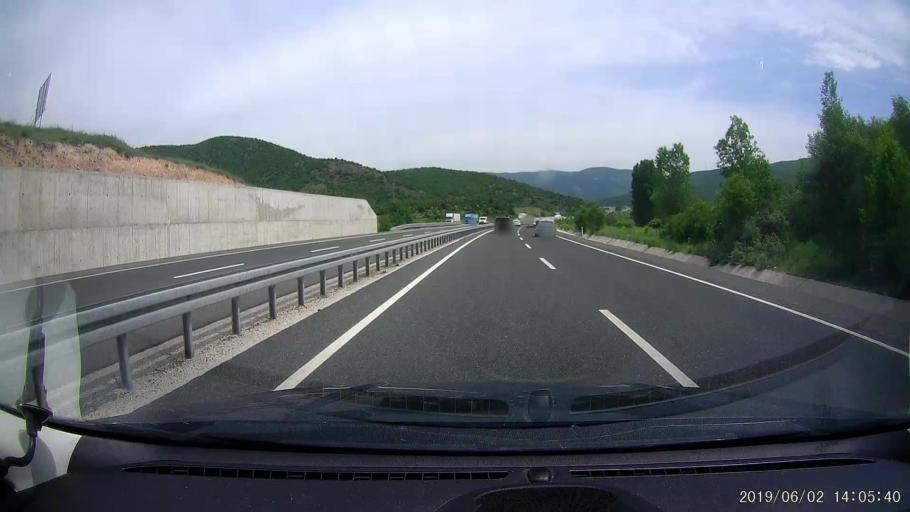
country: TR
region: Cankiri
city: Ilgaz
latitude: 40.8988
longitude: 33.6728
